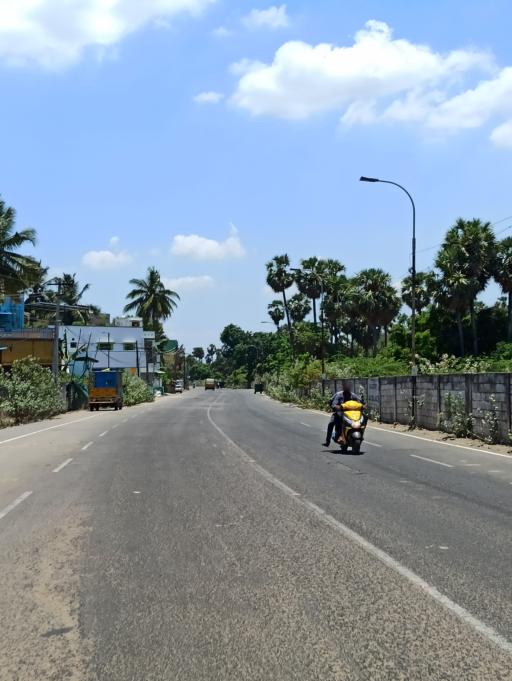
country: IN
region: Tamil Nadu
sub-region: Thiruvallur
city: Chinnasekkadu
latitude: 13.1554
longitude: 80.2387
